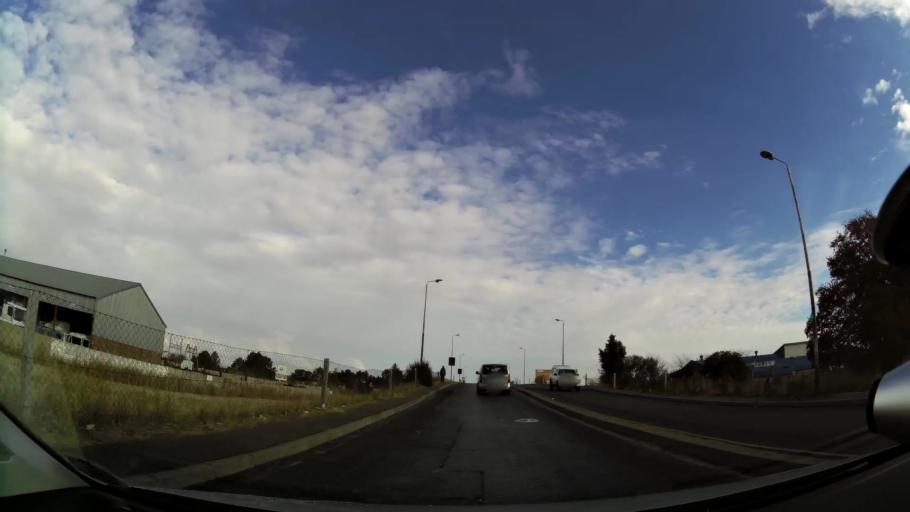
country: ZA
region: Orange Free State
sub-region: Lejweleputswa District Municipality
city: Welkom
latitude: -27.9763
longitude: 26.7624
